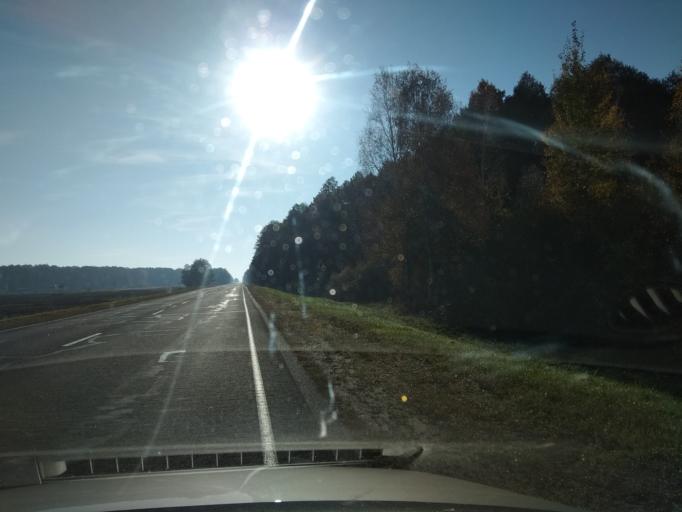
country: BY
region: Brest
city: Malaryta
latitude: 51.8802
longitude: 24.1635
